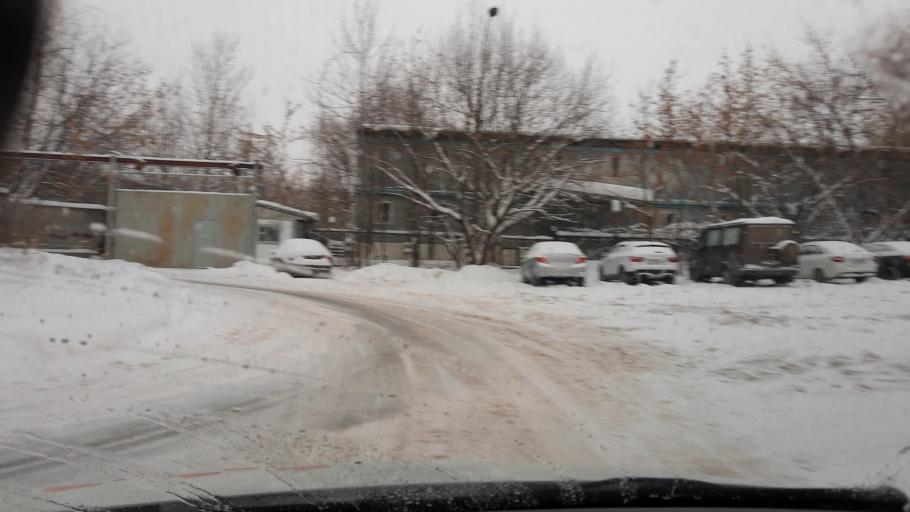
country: RU
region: Moscow
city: Ramenki
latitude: 55.6910
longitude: 37.5075
